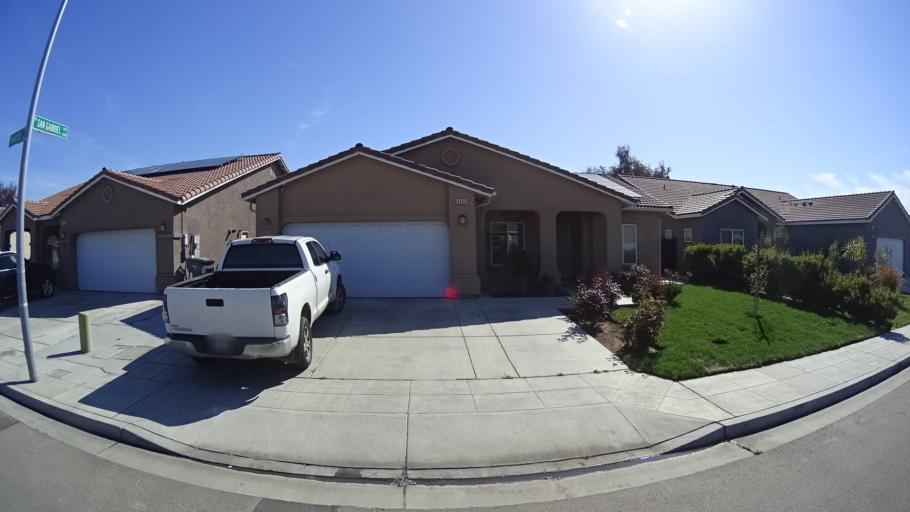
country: US
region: California
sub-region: Fresno County
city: West Park
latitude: 36.8029
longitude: -119.8854
